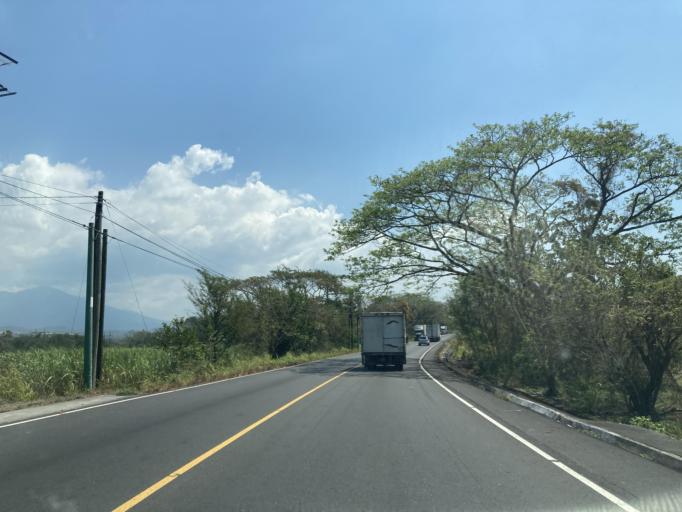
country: GT
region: Santa Rosa
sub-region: Municipio de Taxisco
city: Taxisco
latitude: 14.0971
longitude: -90.5957
